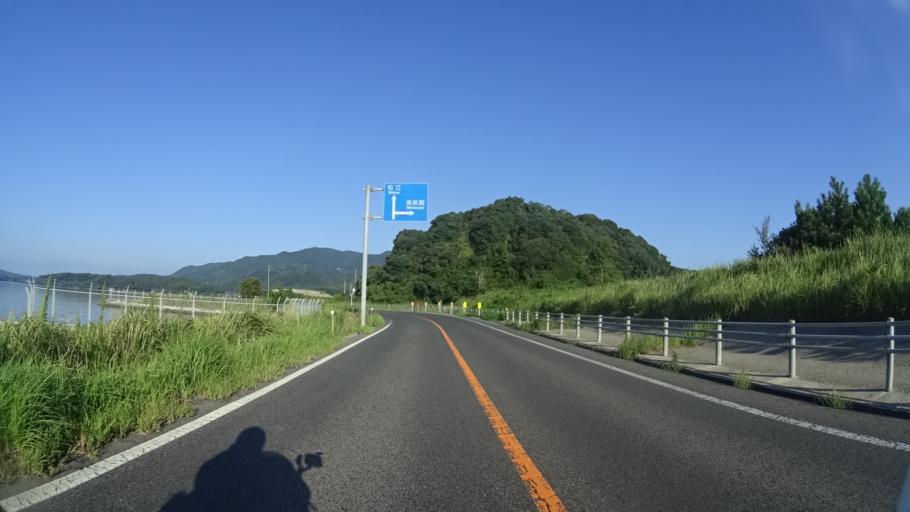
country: JP
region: Shimane
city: Sakaiminato
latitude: 35.5306
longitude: 133.1650
